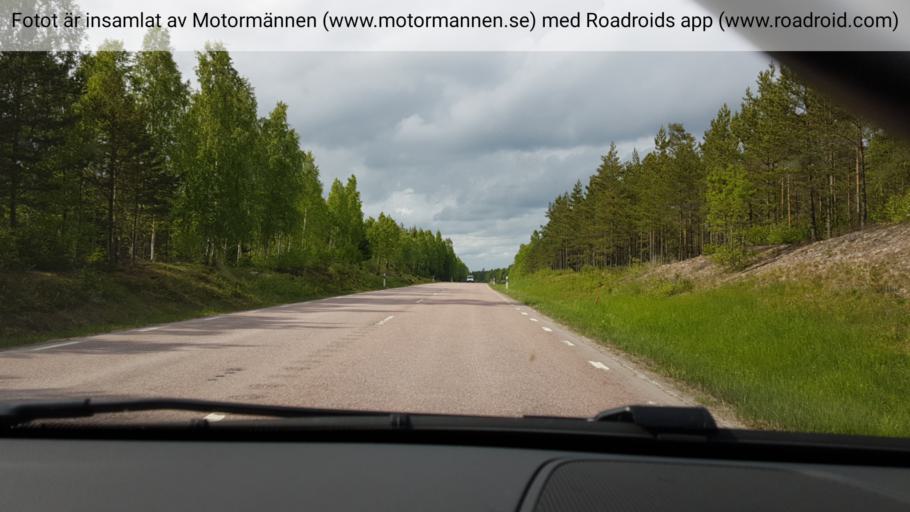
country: SE
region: Uppsala
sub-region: Tierps Kommun
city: Tierp
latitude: 60.2840
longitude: 17.5889
